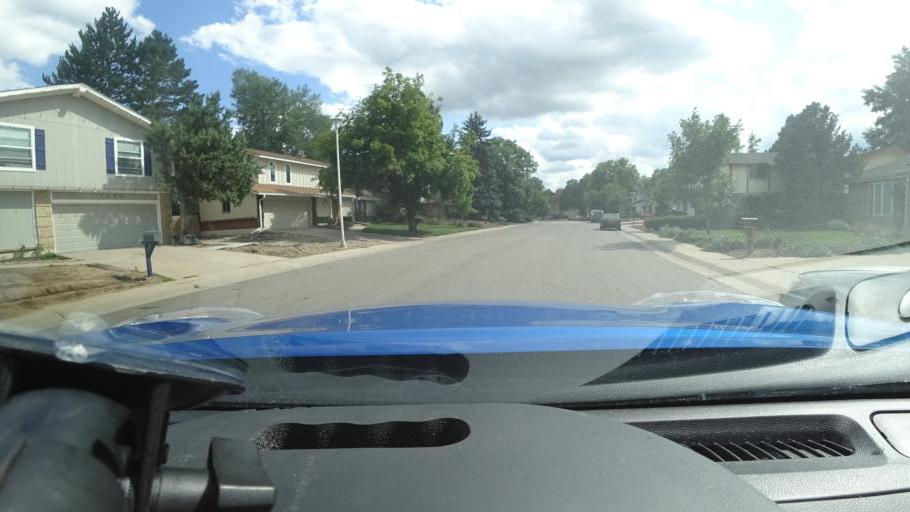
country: US
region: Colorado
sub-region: Adams County
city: Aurora
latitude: 39.6869
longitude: -104.8529
